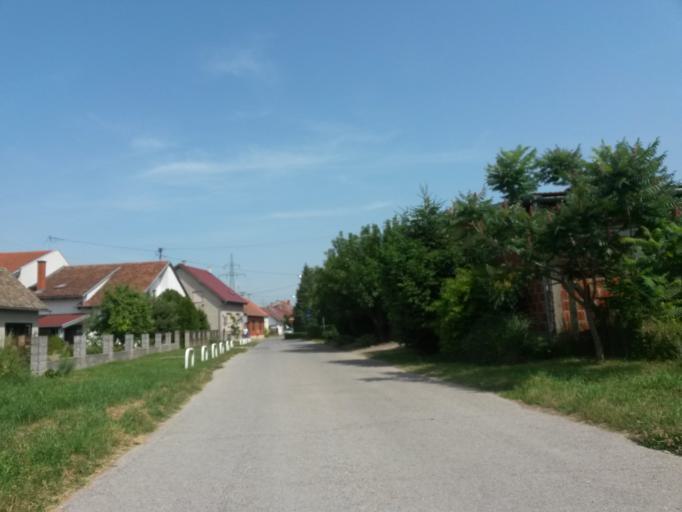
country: HR
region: Osjecko-Baranjska
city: Brijest
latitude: 45.5427
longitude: 18.6654
